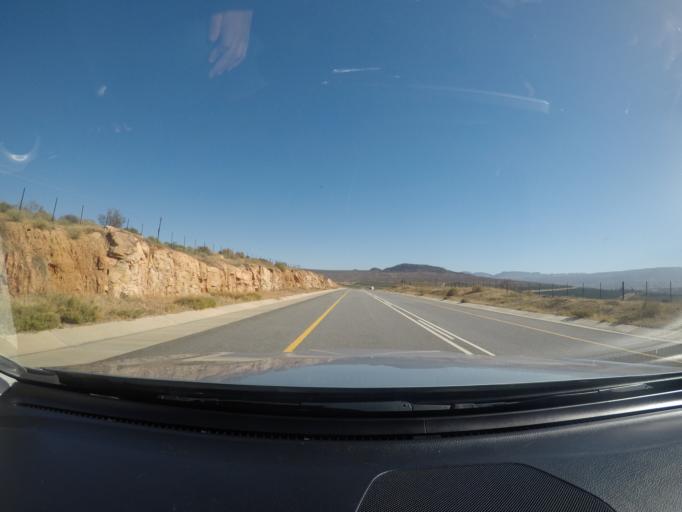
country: ZA
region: Western Cape
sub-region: West Coast District Municipality
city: Clanwilliam
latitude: -32.2094
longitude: 18.8593
